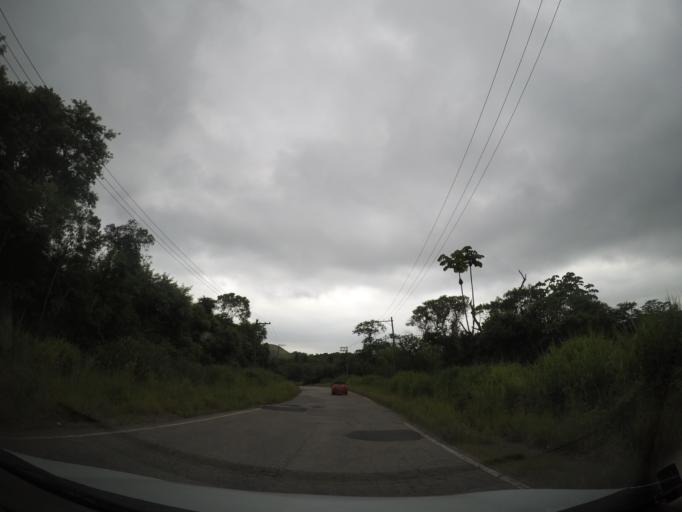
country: BR
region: Sao Paulo
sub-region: Aruja
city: Aruja
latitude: -23.3379
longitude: -46.4025
